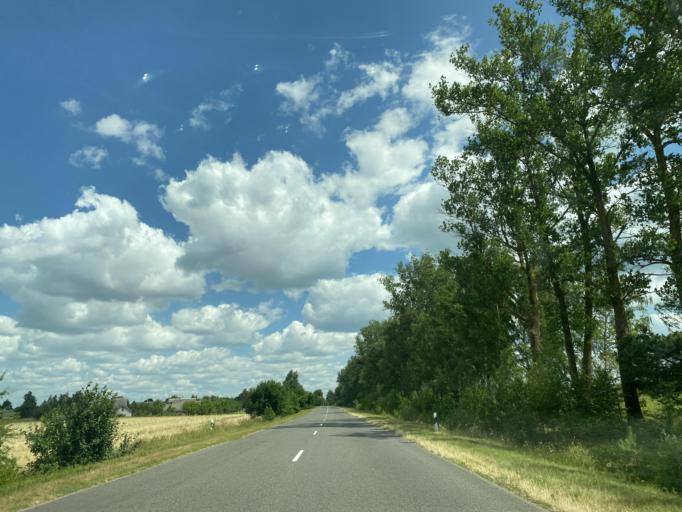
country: BY
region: Brest
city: Ivanava
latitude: 52.1783
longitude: 25.5963
